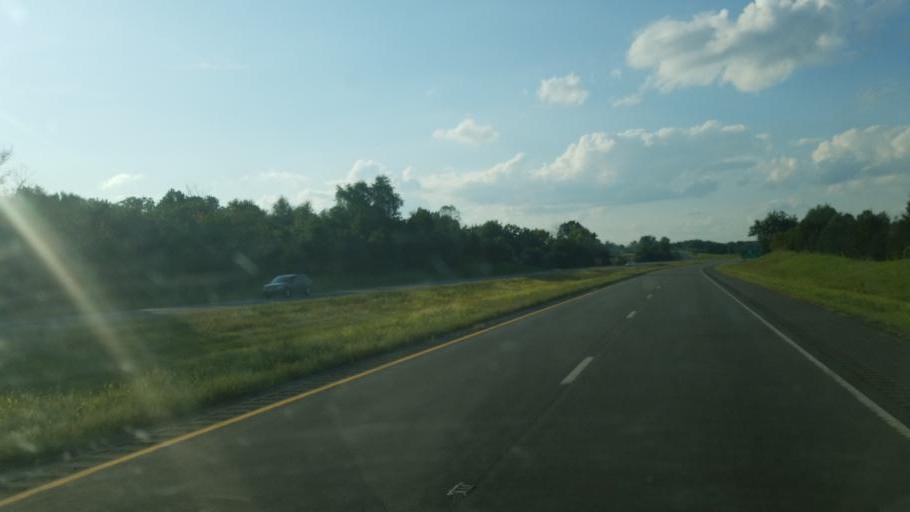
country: US
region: Ohio
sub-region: Knox County
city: Fredericktown
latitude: 40.4722
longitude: -82.5536
